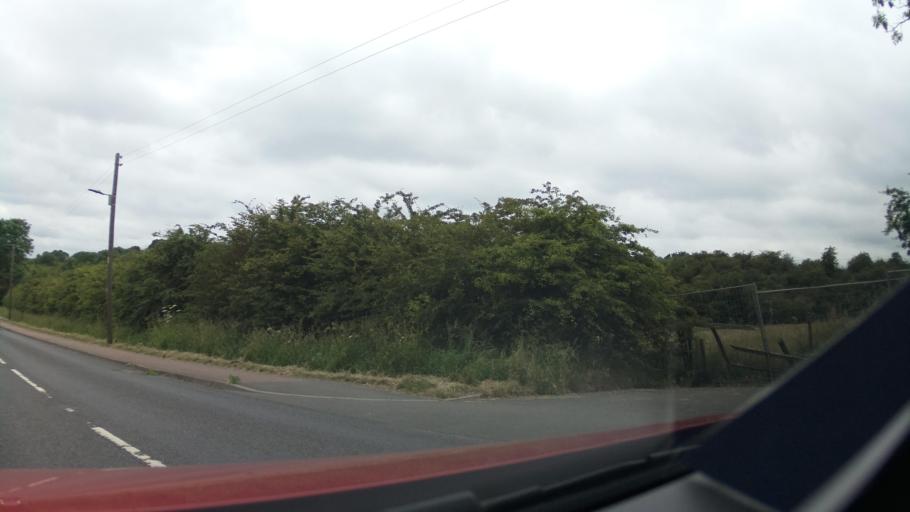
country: GB
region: England
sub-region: Leicestershire
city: Asfordby
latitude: 52.7661
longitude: -0.9333
